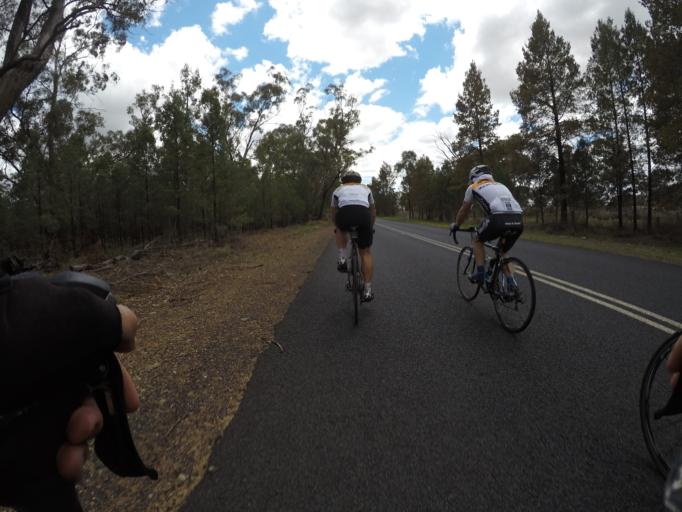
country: AU
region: New South Wales
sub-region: Dubbo Municipality
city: Dubbo
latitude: -32.4849
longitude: 148.5573
